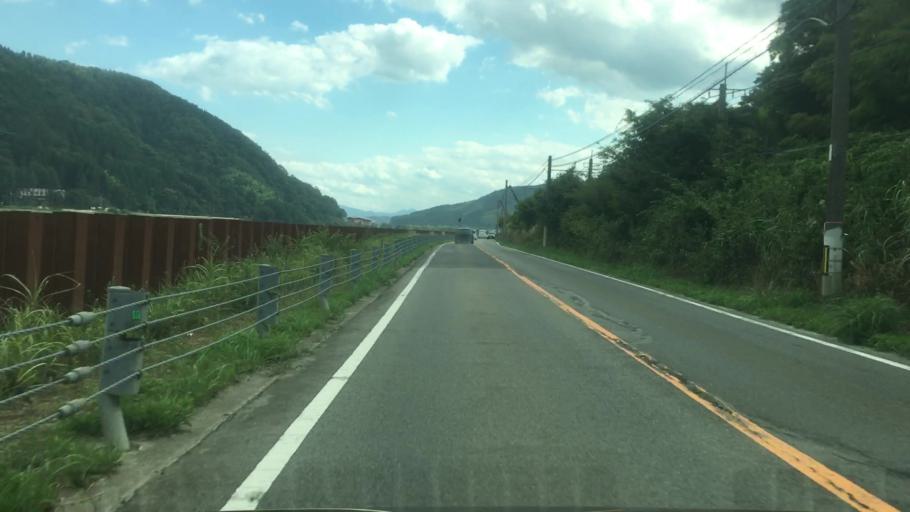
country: JP
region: Hyogo
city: Toyooka
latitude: 35.5995
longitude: 134.8018
